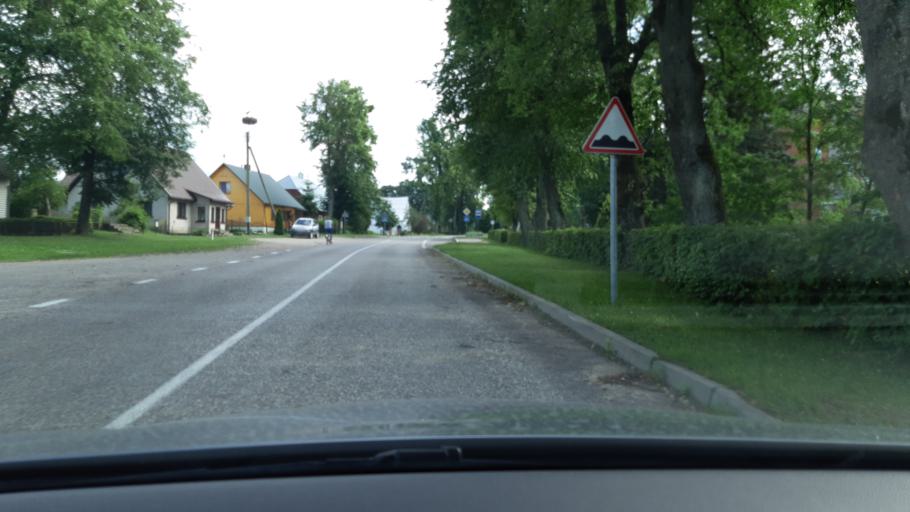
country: LT
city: Kybartai
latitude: 54.4581
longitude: 22.7107
